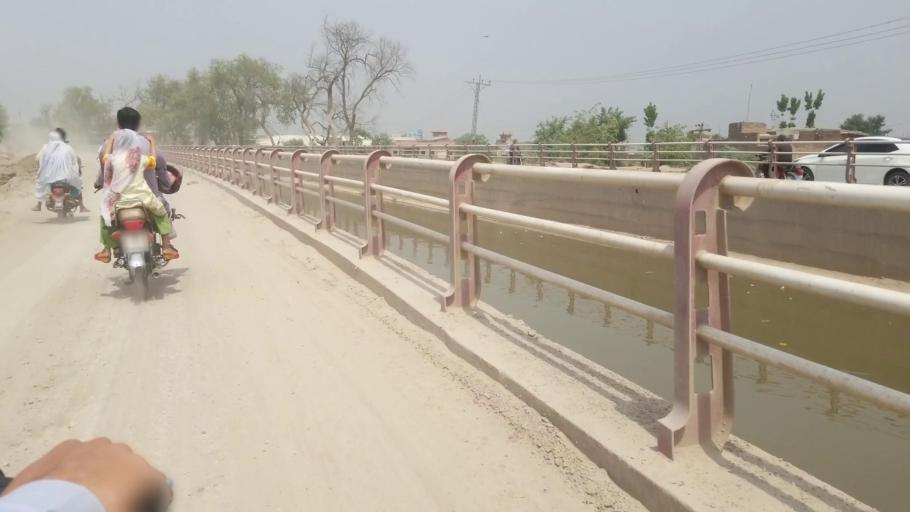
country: PK
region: Khyber Pakhtunkhwa
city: Peshawar
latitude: 33.9663
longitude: 71.5414
